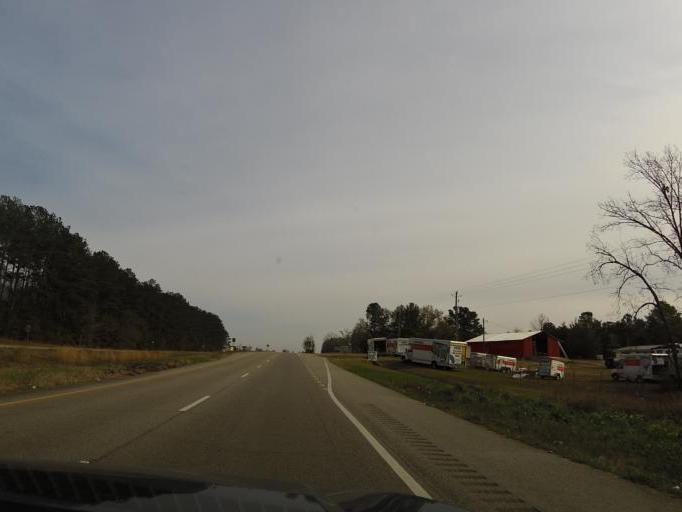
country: US
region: Alabama
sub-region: Houston County
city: Ashford
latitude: 31.1422
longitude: -85.1549
